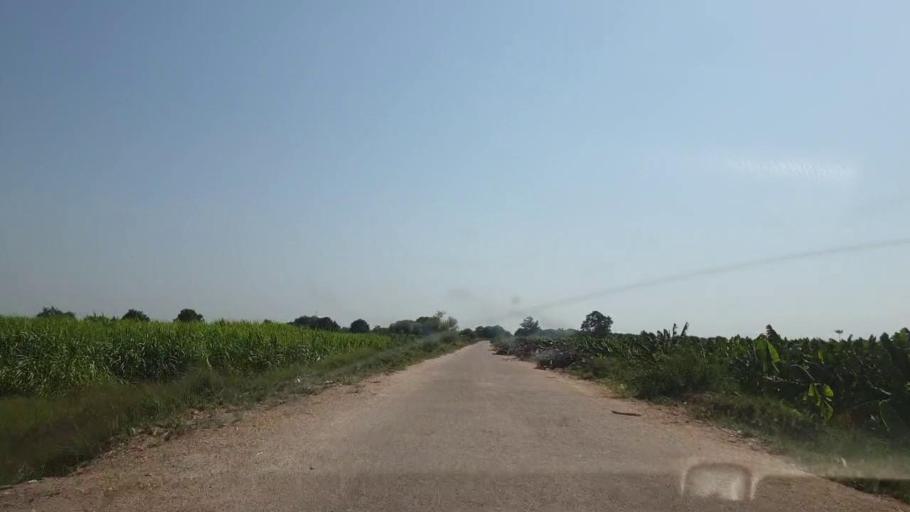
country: PK
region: Sindh
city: Tando Jam
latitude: 25.4195
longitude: 68.5819
